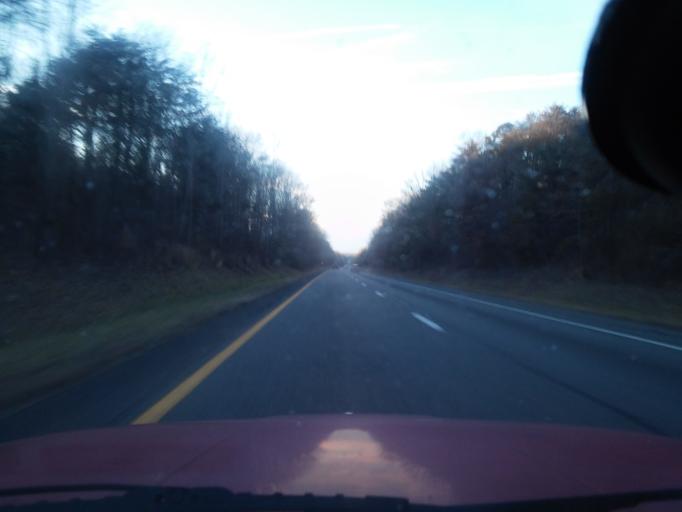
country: US
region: Virginia
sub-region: Goochland County
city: Goochland
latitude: 37.8068
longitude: -77.9277
